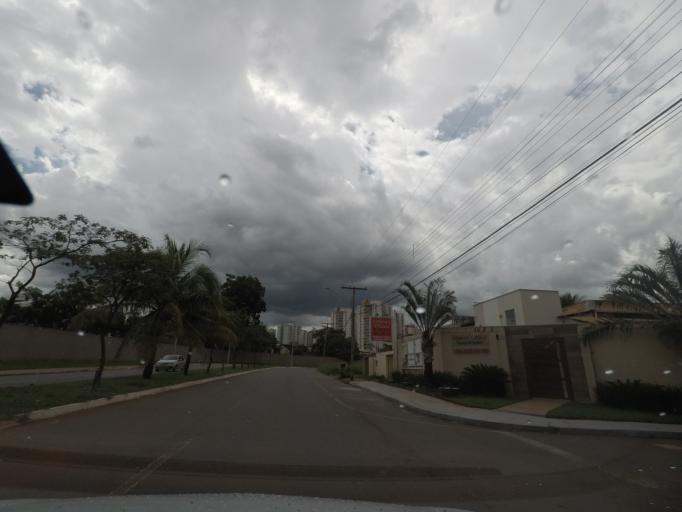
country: BR
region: Goias
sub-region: Goiania
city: Goiania
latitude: -16.7133
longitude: -49.3247
